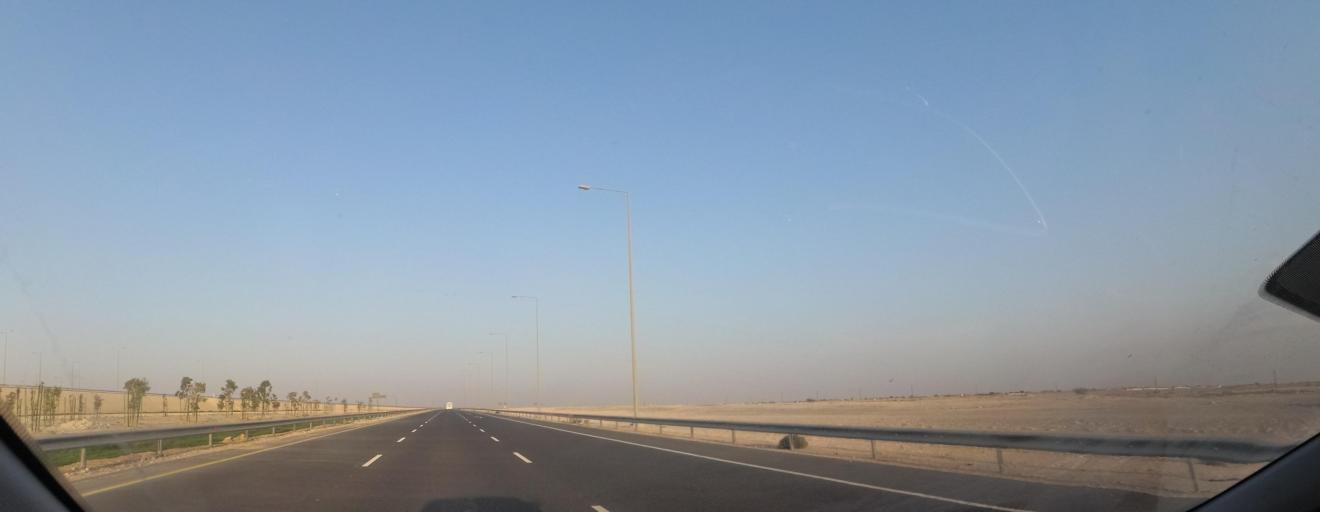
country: QA
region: Baladiyat az Za`ayin
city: Az Za`ayin
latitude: 25.6159
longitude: 51.3707
